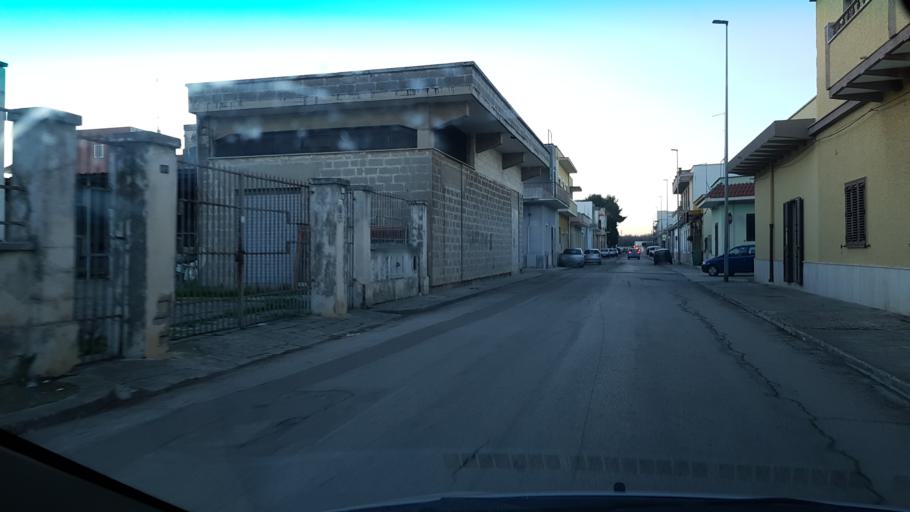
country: IT
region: Apulia
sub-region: Provincia di Brindisi
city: San Pietro Vernotico
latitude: 40.4929
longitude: 17.9931
